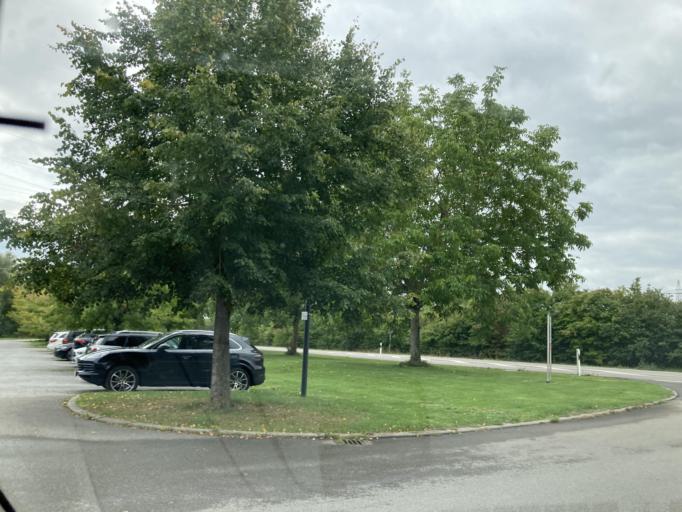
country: DE
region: Baden-Wuerttemberg
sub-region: Regierungsbezirk Stuttgart
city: Bondorf
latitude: 48.5278
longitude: 8.8074
